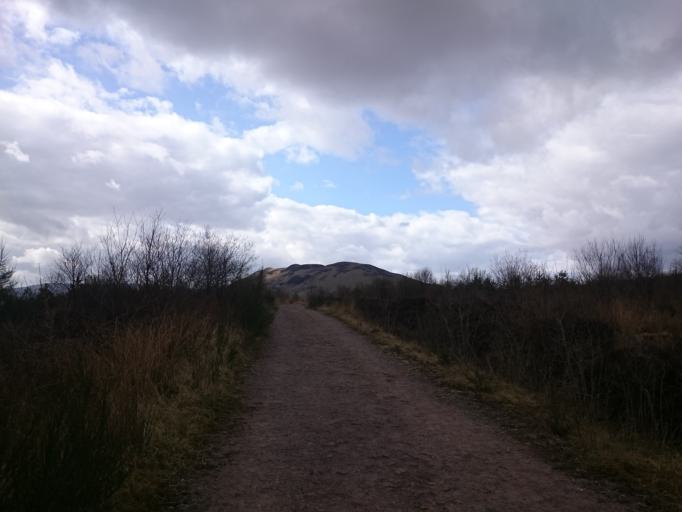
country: GB
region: Scotland
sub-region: Stirling
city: Killearn
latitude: 56.0918
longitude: -4.4848
